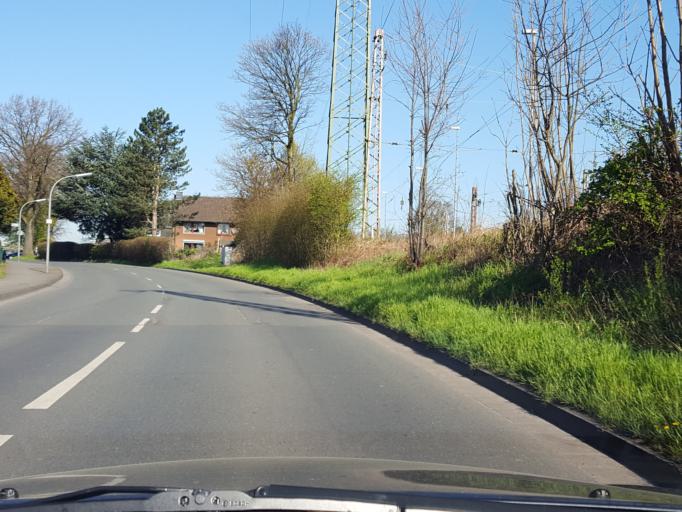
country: DE
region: North Rhine-Westphalia
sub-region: Regierungsbezirk Munster
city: Recklinghausen
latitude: 51.6687
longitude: 7.1715
